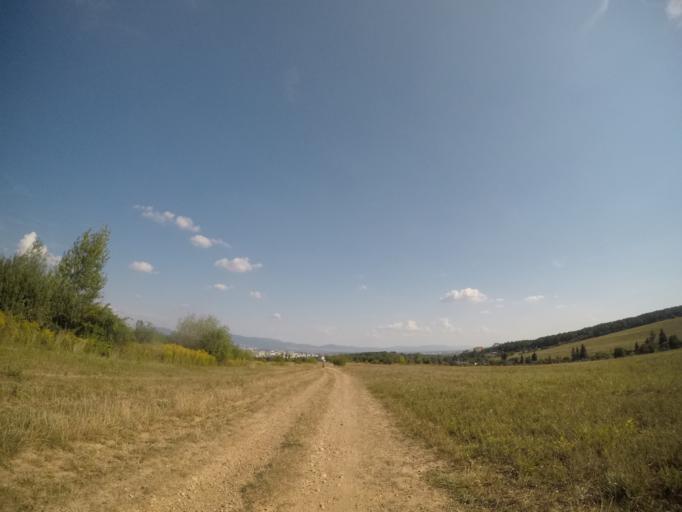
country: SK
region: Kosicky
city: Kosice
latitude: 48.7300
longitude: 21.2161
